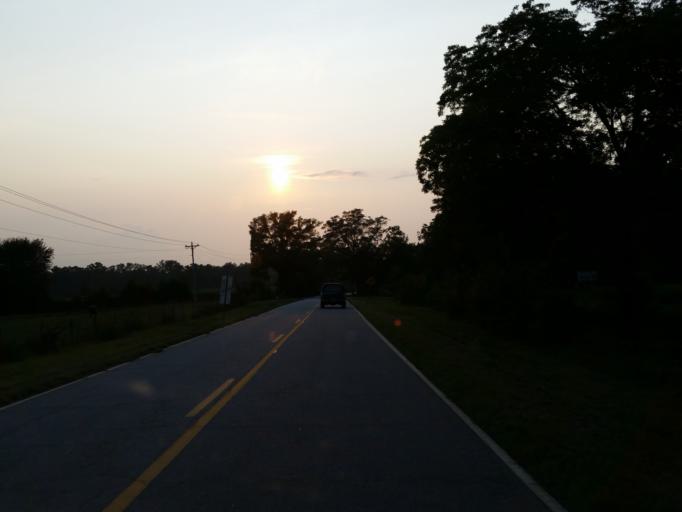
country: US
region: Georgia
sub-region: Henry County
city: Locust Grove
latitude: 33.2754
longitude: -84.1403
